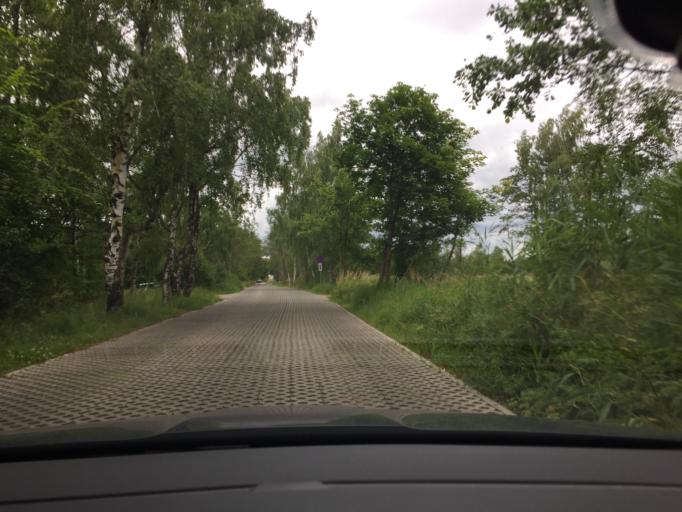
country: PL
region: Pomeranian Voivodeship
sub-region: Gdansk
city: Gdansk
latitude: 54.3656
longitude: 18.7712
